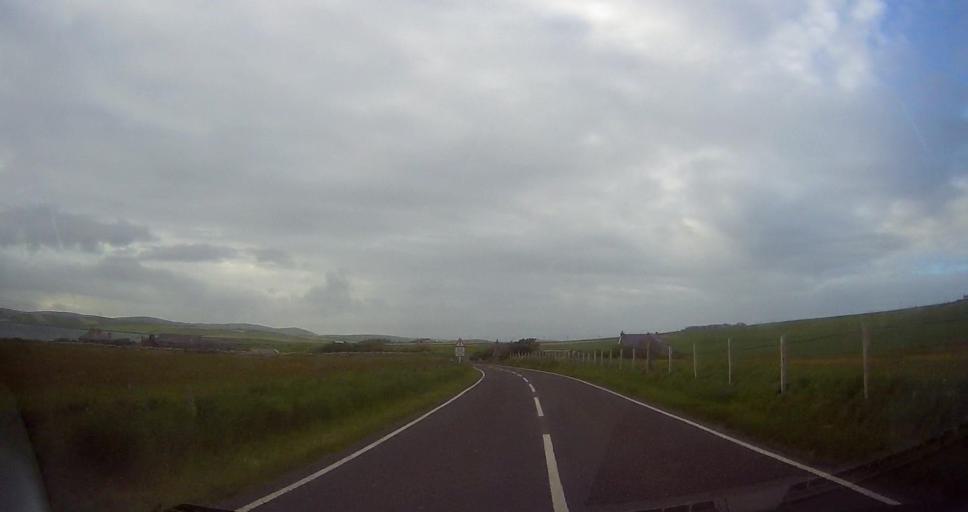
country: GB
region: Scotland
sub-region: Orkney Islands
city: Stromness
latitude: 58.9672
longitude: -3.2266
